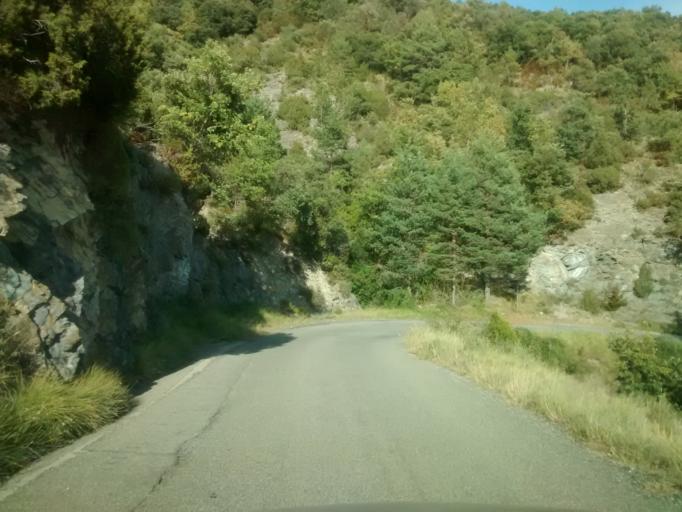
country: ES
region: Aragon
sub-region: Provincia de Huesca
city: Puertolas
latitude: 42.5649
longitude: 0.1718
